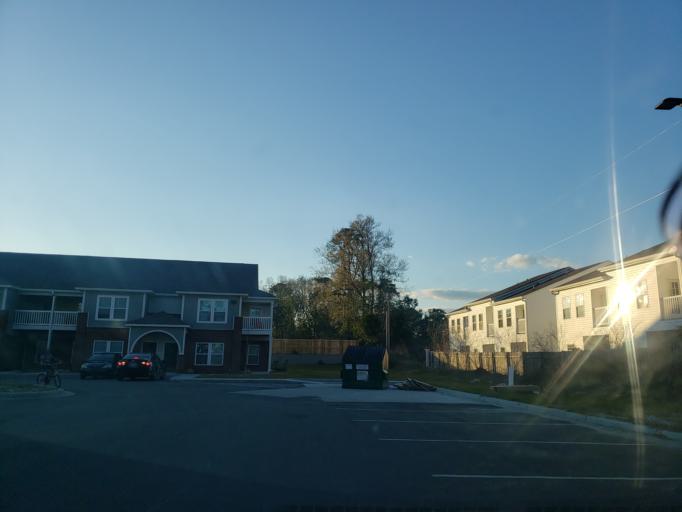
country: US
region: Georgia
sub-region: Chatham County
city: Montgomery
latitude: 31.9997
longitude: -81.1349
